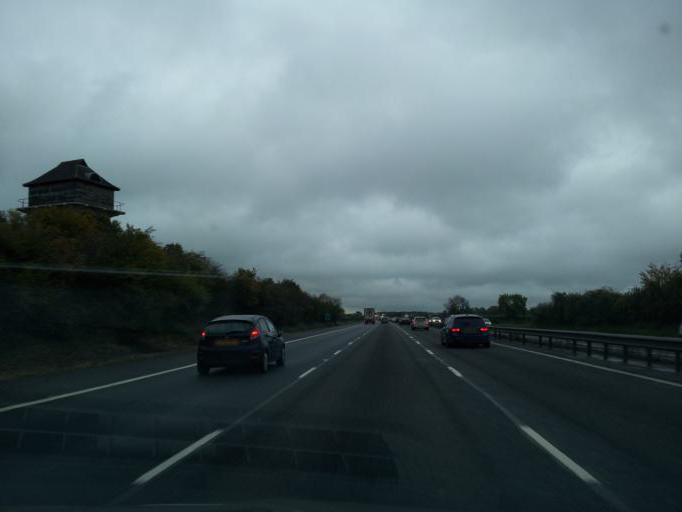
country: GB
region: England
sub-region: Oxfordshire
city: Bicester
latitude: 51.9183
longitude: -1.2033
